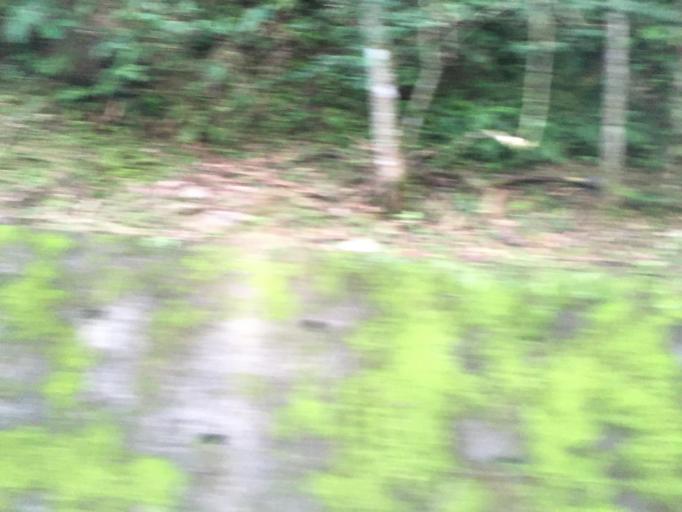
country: TW
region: Taiwan
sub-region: Yilan
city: Yilan
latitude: 24.7560
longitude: 121.5963
